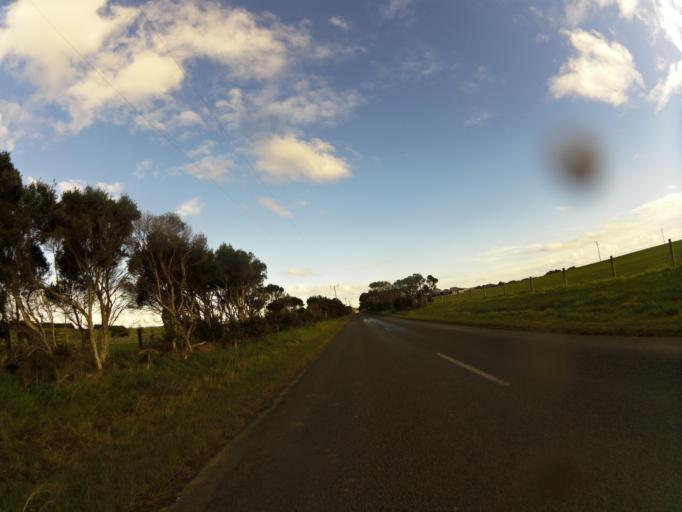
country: AU
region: Victoria
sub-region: Bass Coast
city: North Wonthaggi
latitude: -38.5547
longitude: 145.5492
